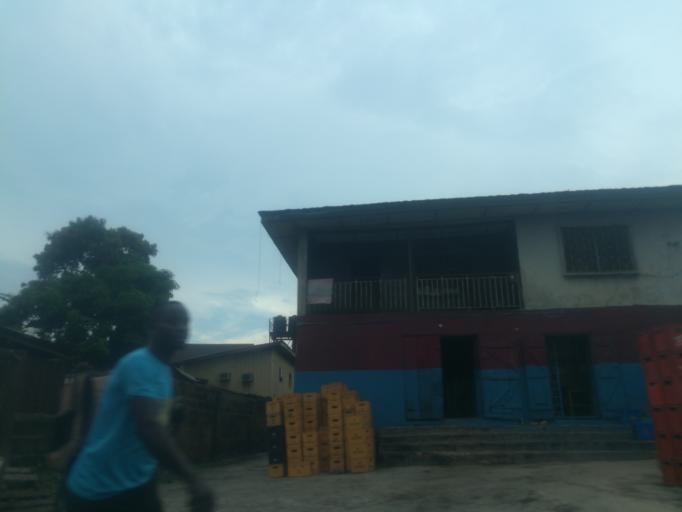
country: NG
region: Oyo
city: Moniya
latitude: 7.4548
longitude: 3.9085
